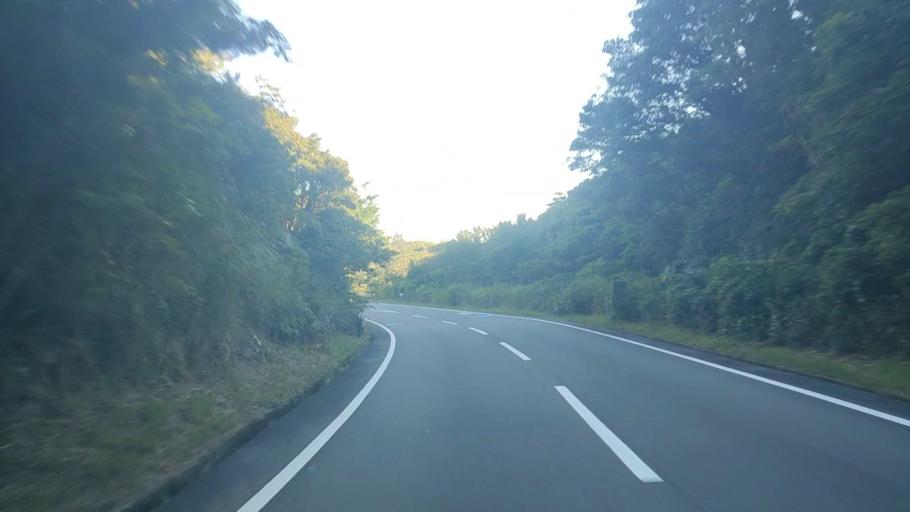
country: JP
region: Mie
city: Toba
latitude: 34.4195
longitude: 136.9140
